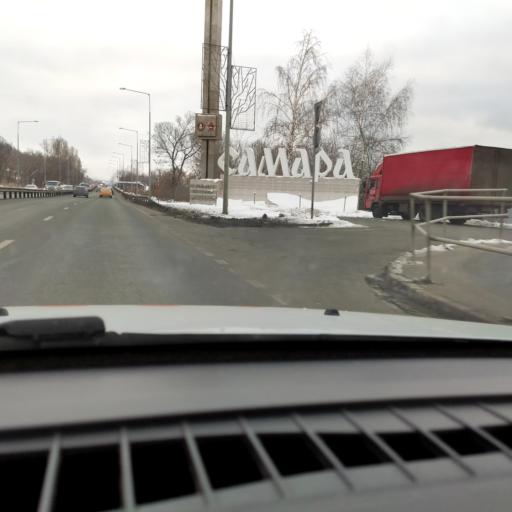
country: RU
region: Samara
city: Volzhskiy
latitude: 53.4069
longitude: 50.1438
